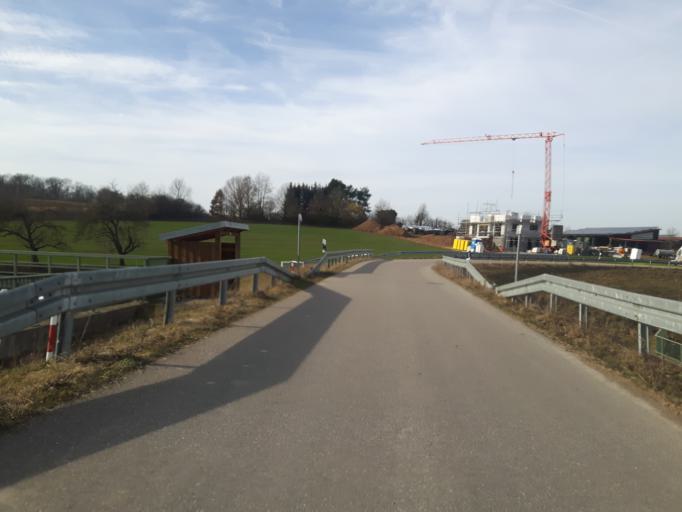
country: DE
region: Baden-Wuerttemberg
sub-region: Regierungsbezirk Stuttgart
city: Bretzfeld
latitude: 49.1578
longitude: 9.4342
